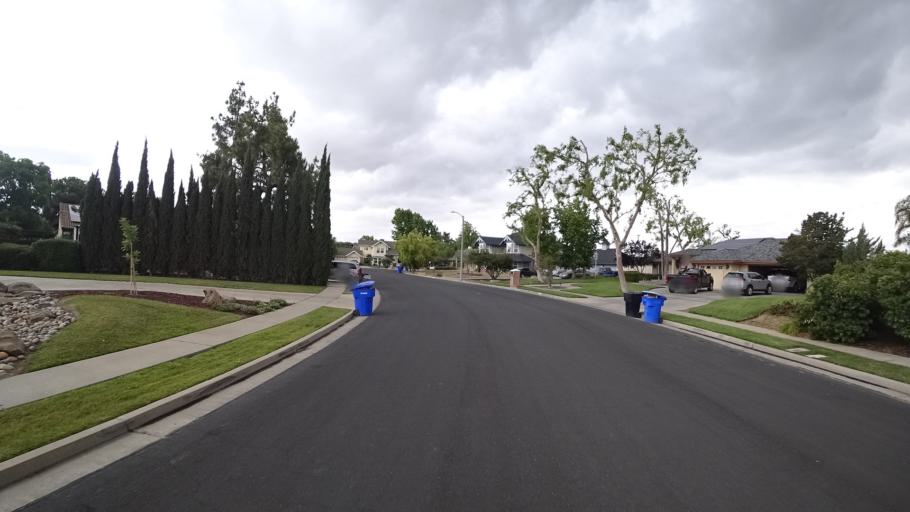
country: US
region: California
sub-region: Kings County
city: Hanford
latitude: 36.3356
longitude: -119.6623
